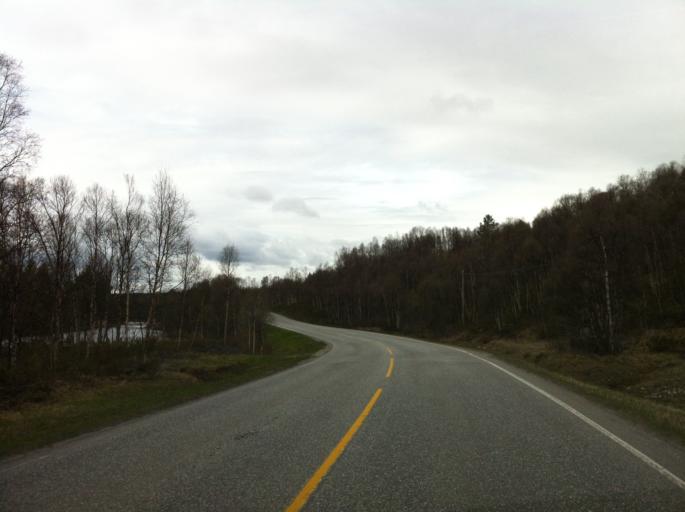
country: NO
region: Sor-Trondelag
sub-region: Roros
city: Roros
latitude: 62.5956
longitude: 11.4404
